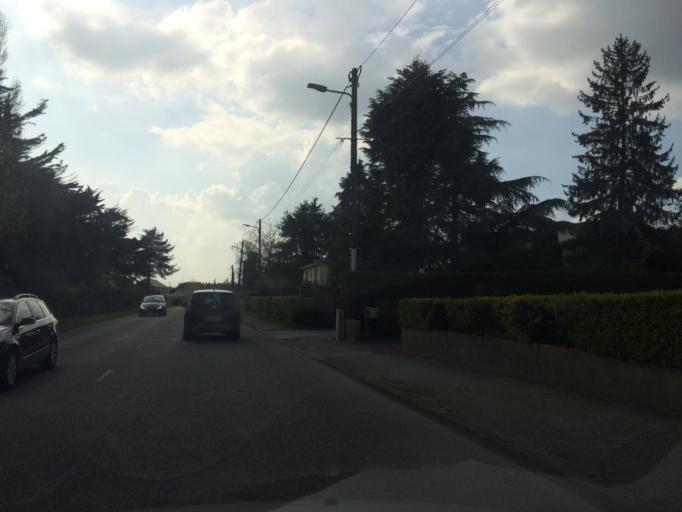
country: FR
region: Pays de la Loire
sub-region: Departement de la Loire-Atlantique
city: Blain
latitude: 47.4784
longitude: -1.7742
